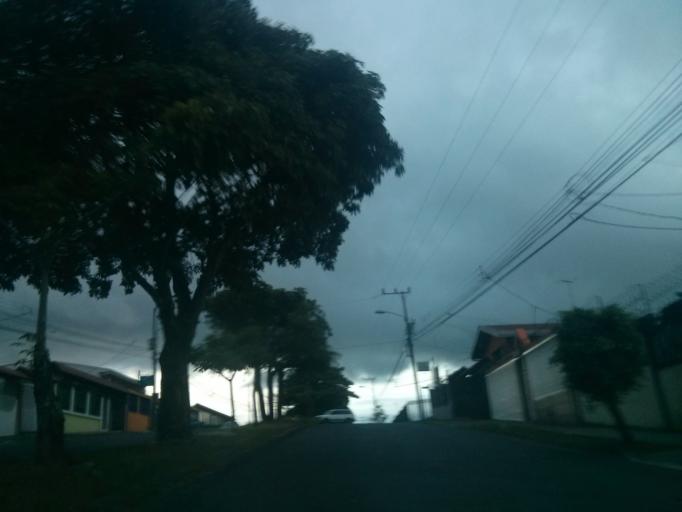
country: CR
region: San Jose
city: San Pedro
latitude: 9.9097
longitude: -84.0609
